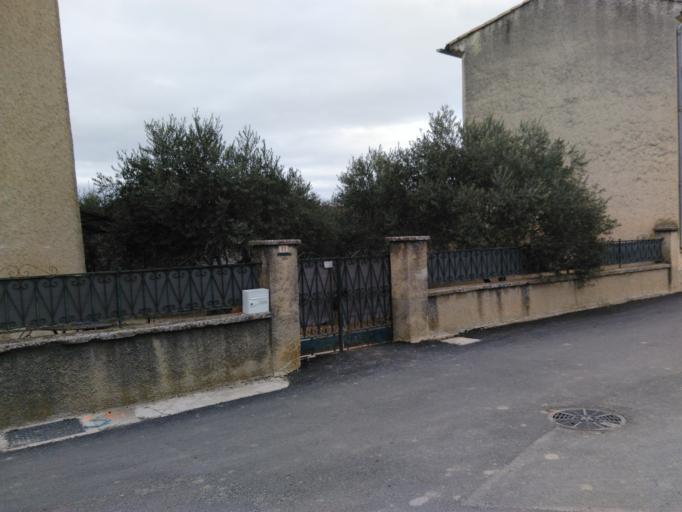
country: FR
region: Provence-Alpes-Cote d'Azur
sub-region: Departement du Vaucluse
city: Malemort-du-Comtat
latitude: 44.0189
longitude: 5.1591
